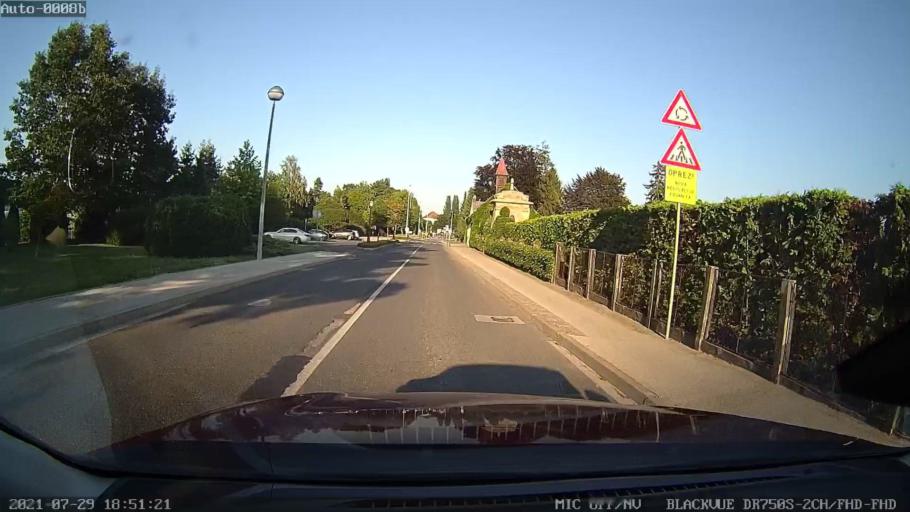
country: HR
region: Varazdinska
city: Varazdin
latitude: 46.3103
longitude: 16.3249
